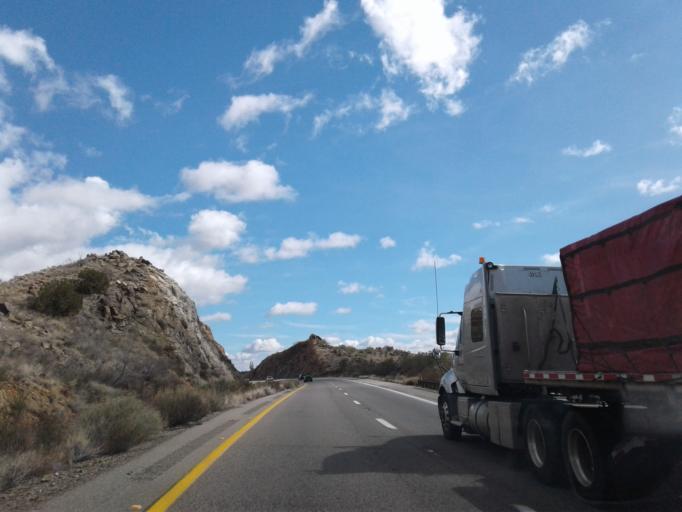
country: US
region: Arizona
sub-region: Yavapai County
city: Bagdad
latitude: 34.4627
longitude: -113.2999
